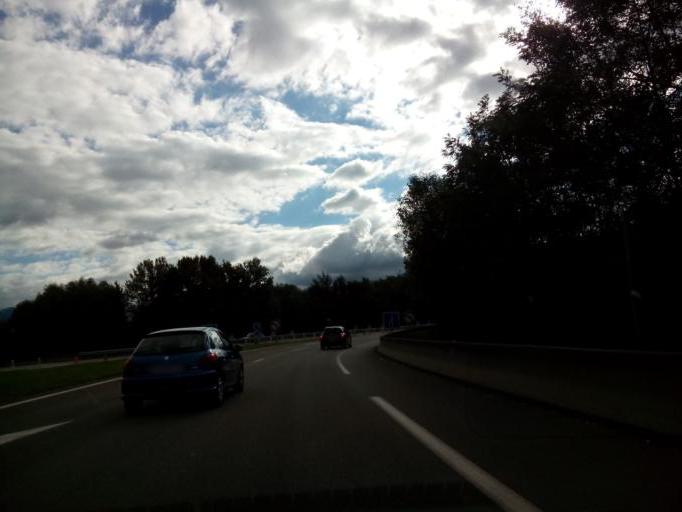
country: FR
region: Rhone-Alpes
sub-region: Departement de la Savoie
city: La Motte-Servolex
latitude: 45.6053
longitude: 5.8828
